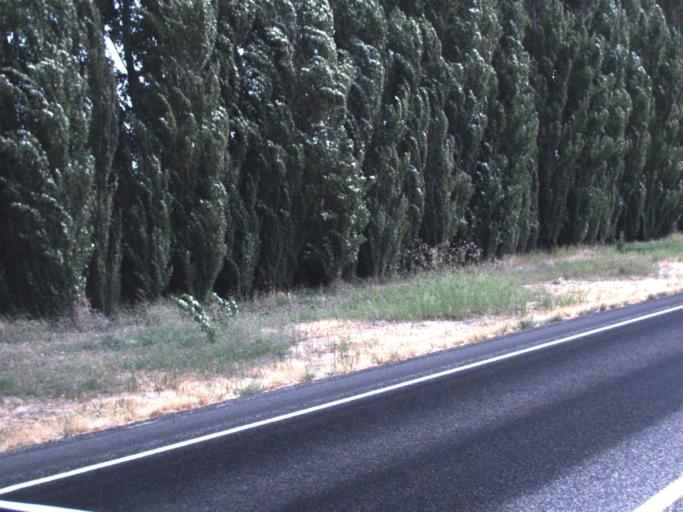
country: US
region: Oregon
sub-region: Morrow County
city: Irrigon
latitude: 45.9486
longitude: -119.6029
